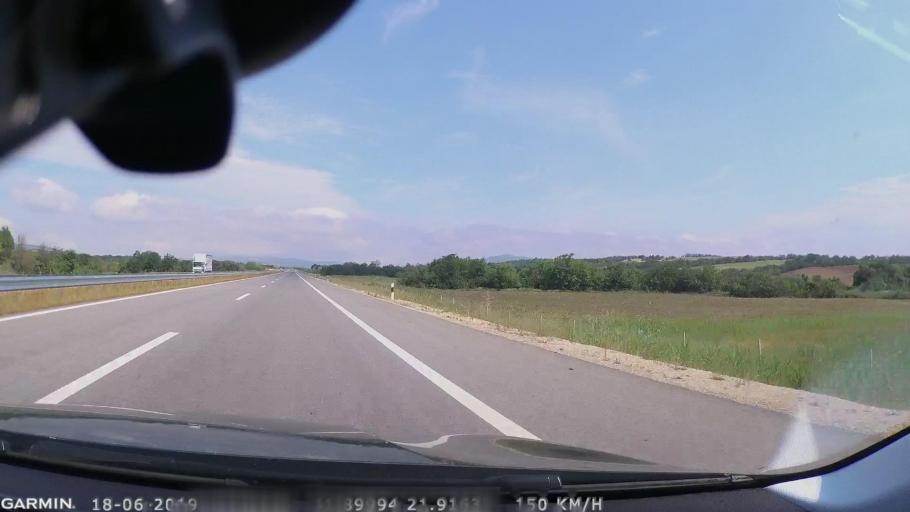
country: MK
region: Sveti Nikole
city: Gorobinci
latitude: 41.9013
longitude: 21.9144
